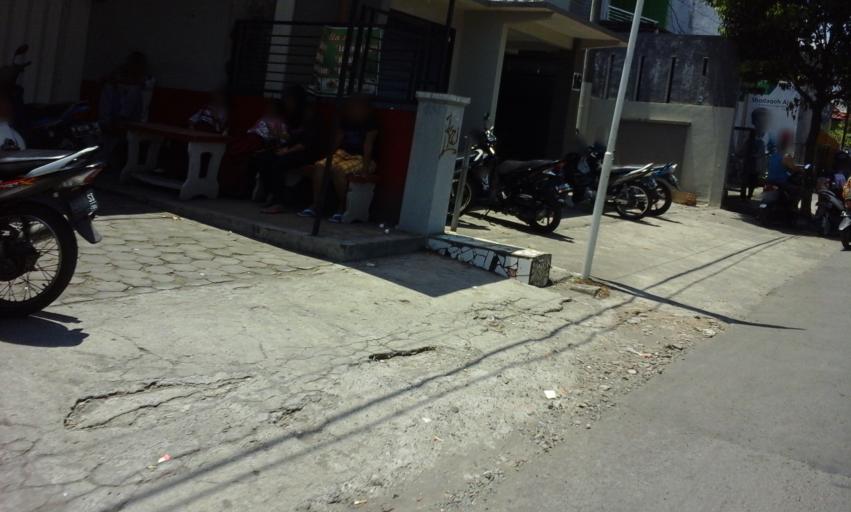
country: ID
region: East Java
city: Sumbersari Wetan
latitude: -8.1809
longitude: 113.7156
